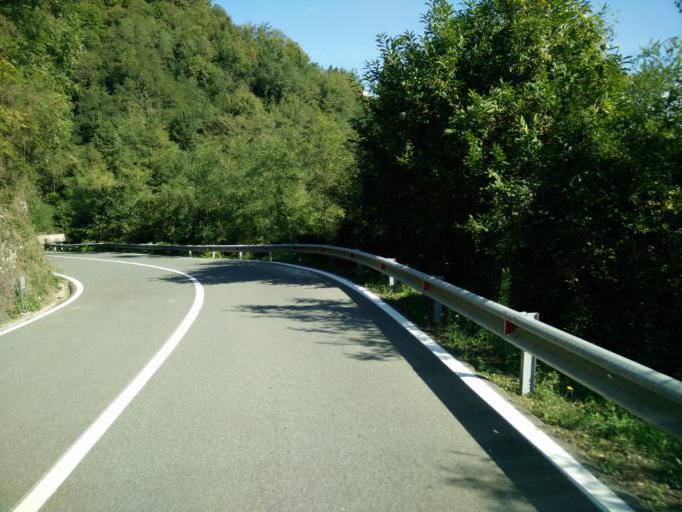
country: IT
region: Liguria
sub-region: Provincia di La Spezia
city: Carrodano
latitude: 44.2446
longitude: 9.6328
